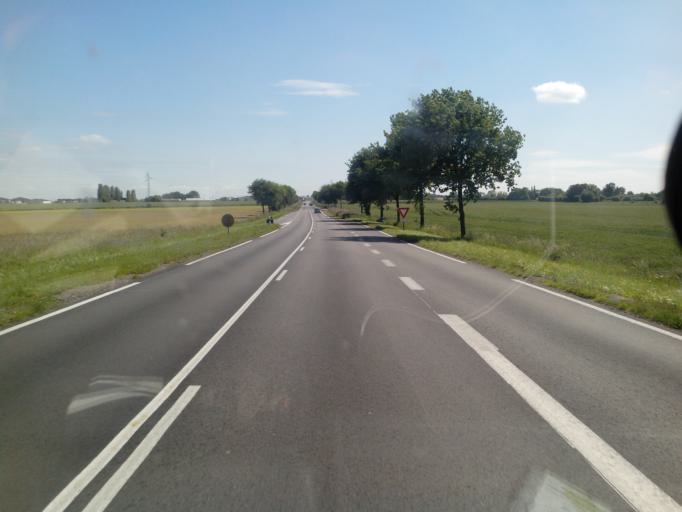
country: FR
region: Haute-Normandie
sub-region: Departement de l'Eure
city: Beuzeville
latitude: 49.3666
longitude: 0.3954
